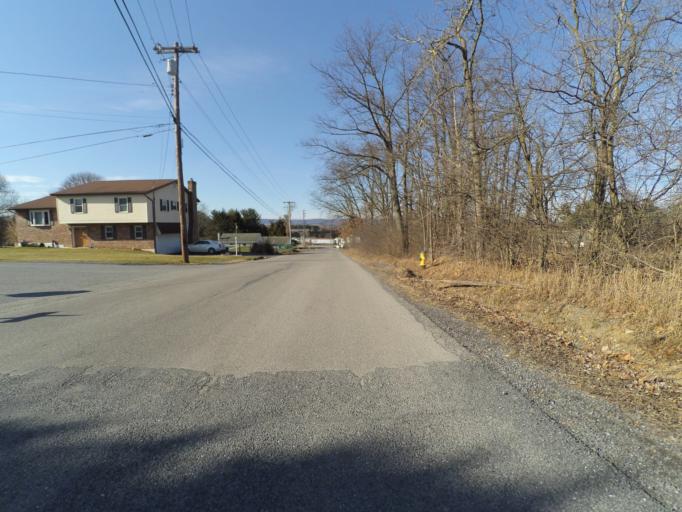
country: US
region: Pennsylvania
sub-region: Centre County
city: Lemont
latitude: 40.8230
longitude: -77.8039
